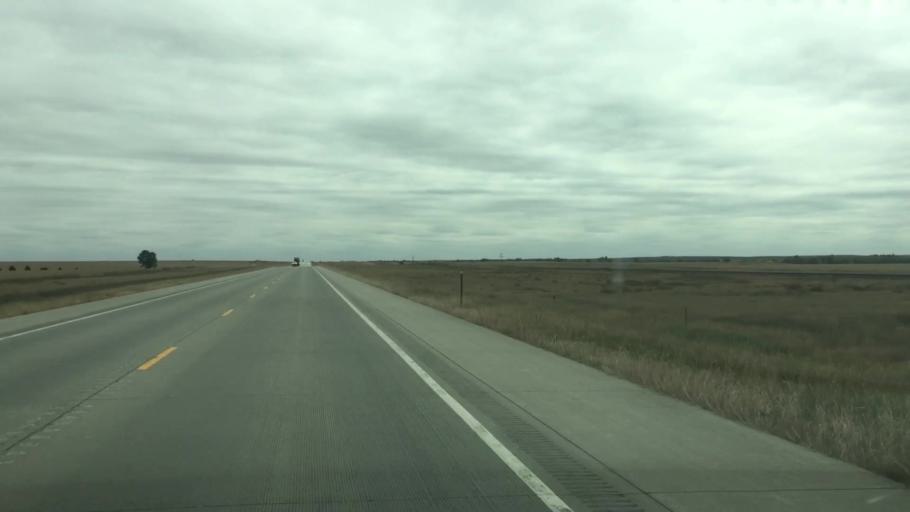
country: US
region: Colorado
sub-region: Kiowa County
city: Eads
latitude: 38.7781
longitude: -102.8920
